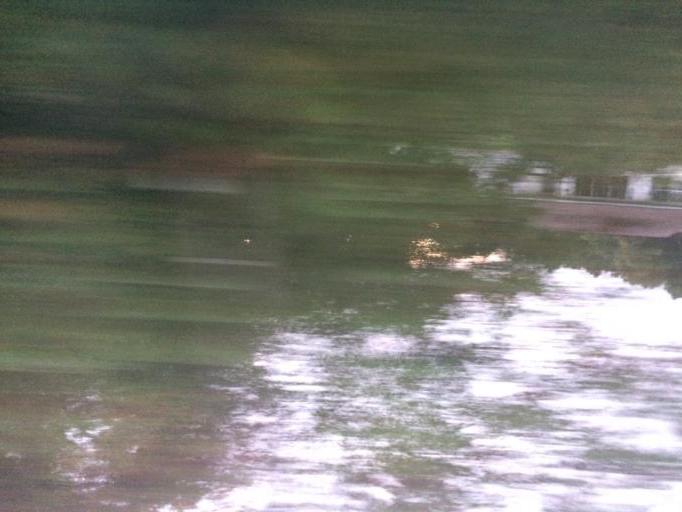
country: US
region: New York
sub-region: Erie County
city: Billington Heights
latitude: 42.7852
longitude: -78.6202
